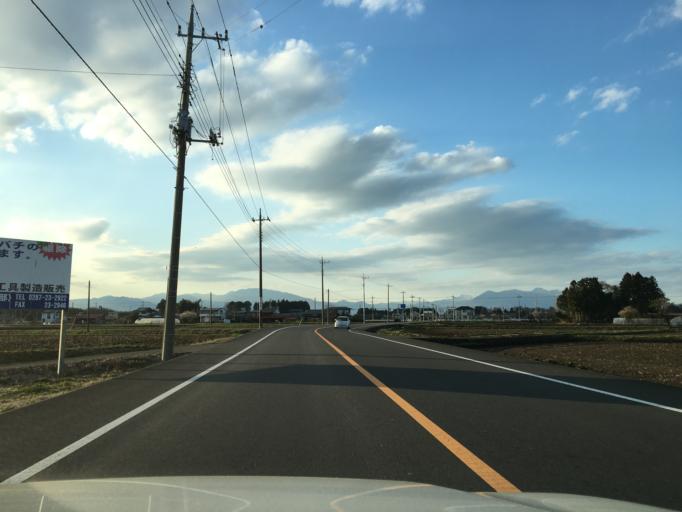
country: JP
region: Tochigi
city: Otawara
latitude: 36.8812
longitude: 140.0644
